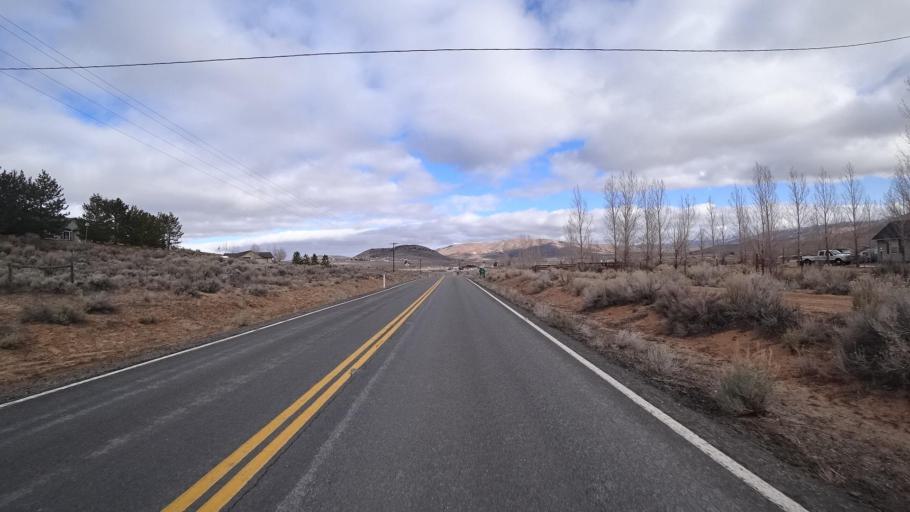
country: US
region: Nevada
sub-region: Washoe County
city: Cold Springs
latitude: 39.8573
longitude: -119.9350
